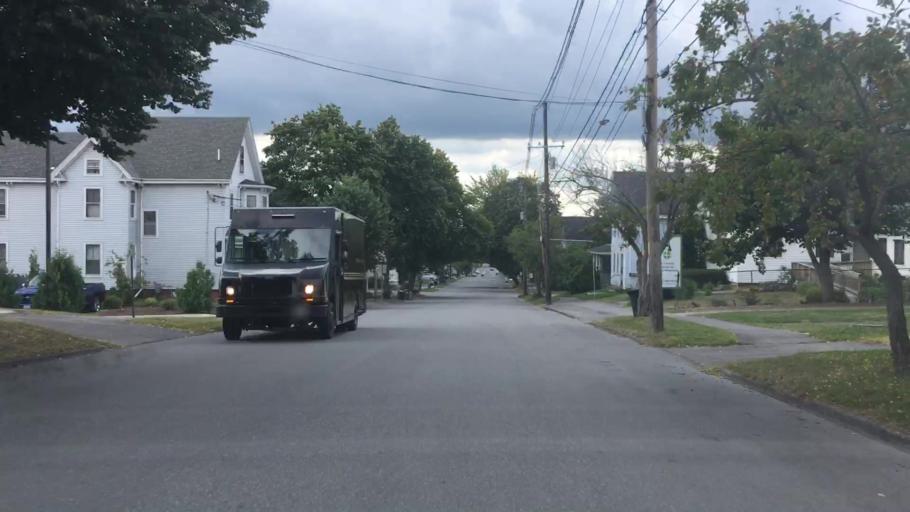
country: US
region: Maine
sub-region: Penobscot County
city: Bangor
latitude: 44.8133
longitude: -68.7731
